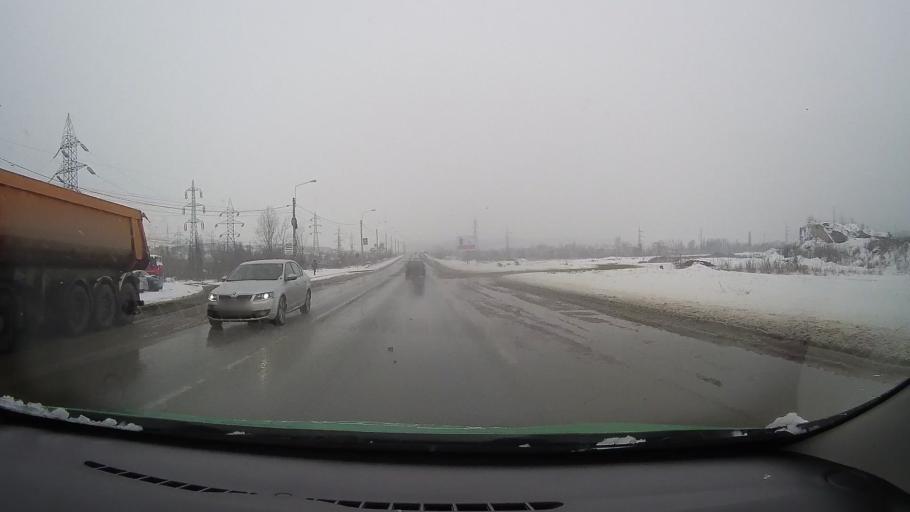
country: RO
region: Hunedoara
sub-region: Municipiul Hunedoara
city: Pestisu Mare
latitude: 45.7812
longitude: 22.9122
